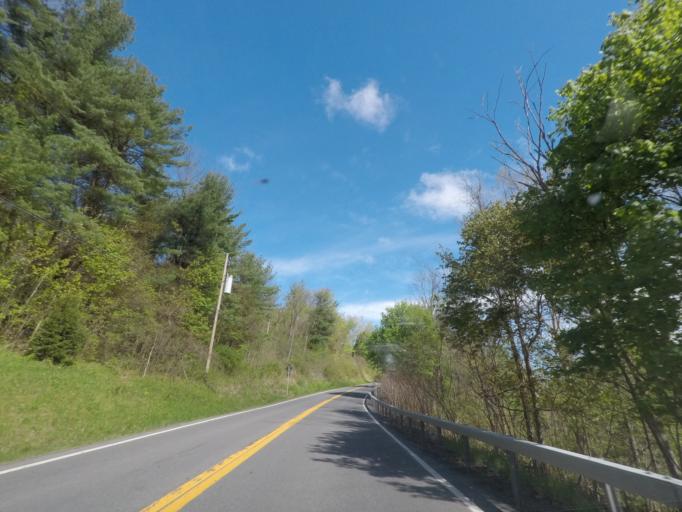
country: US
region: New York
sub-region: Albany County
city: Ravena
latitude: 42.4753
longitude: -73.9243
